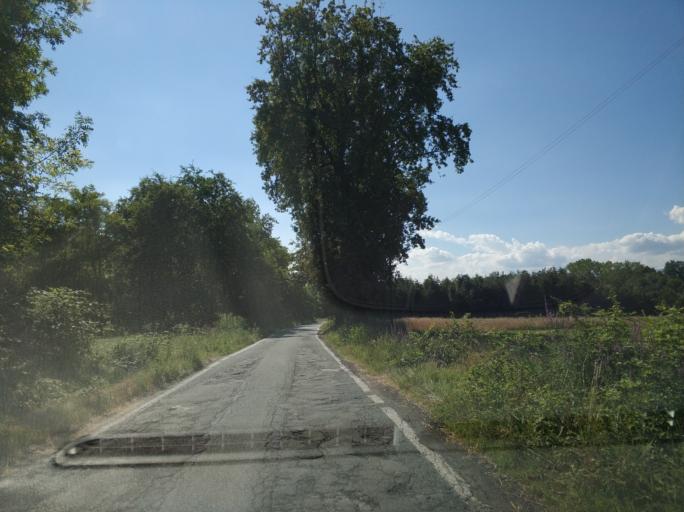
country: IT
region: Piedmont
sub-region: Provincia di Torino
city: Rivarossa
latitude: 45.2400
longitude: 7.7179
